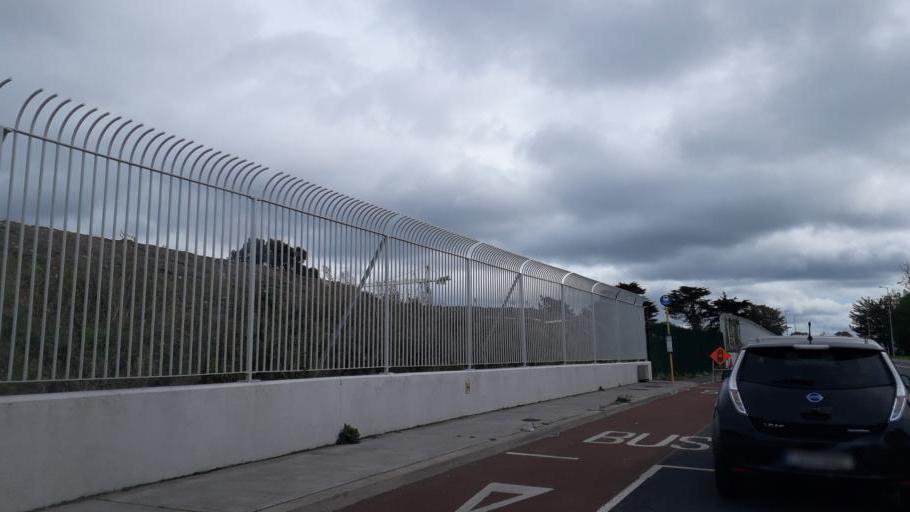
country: IE
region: Leinster
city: Cabinteely
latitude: 53.2761
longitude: -6.1559
